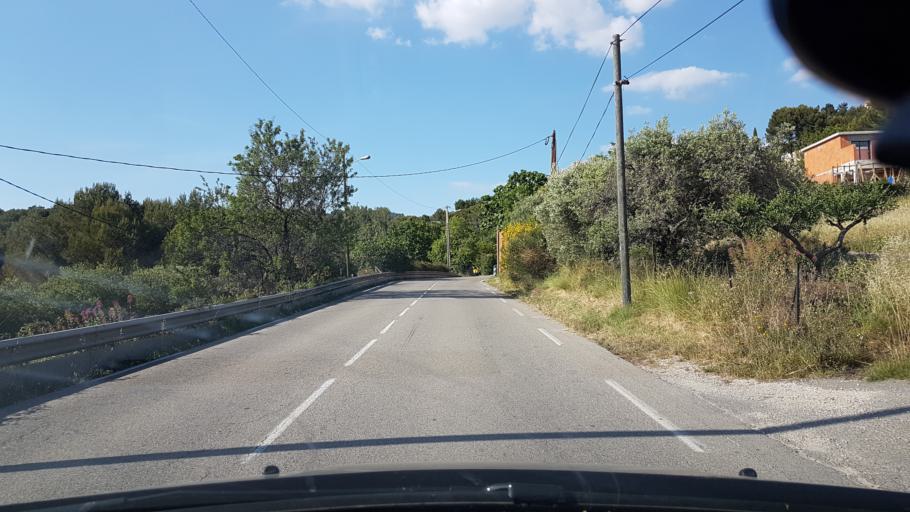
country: FR
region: Provence-Alpes-Cote d'Azur
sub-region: Departement des Bouches-du-Rhone
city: Carnoux-en-Provence
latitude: 43.2399
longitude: 5.5623
